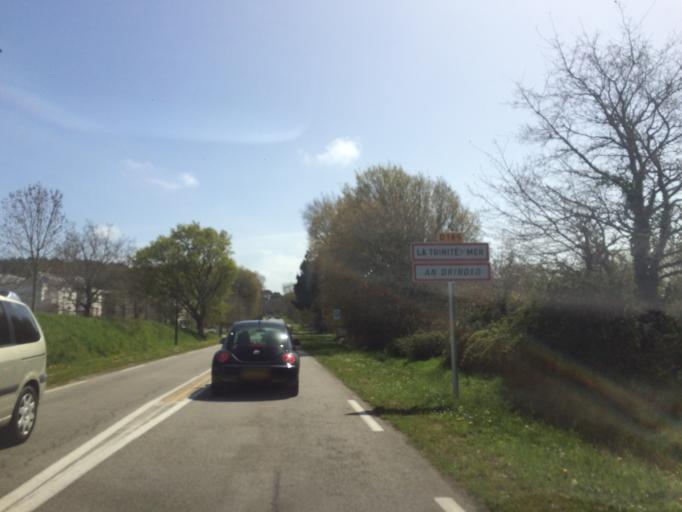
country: FR
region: Brittany
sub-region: Departement du Morbihan
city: La Trinite-sur-Mer
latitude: 47.5939
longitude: -3.0361
